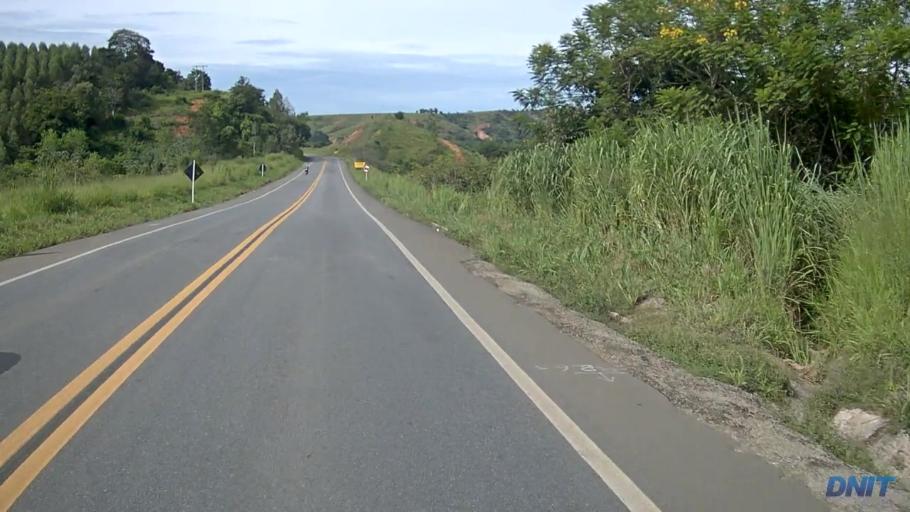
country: BR
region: Minas Gerais
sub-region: Belo Oriente
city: Belo Oriente
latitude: -19.2636
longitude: -42.3458
